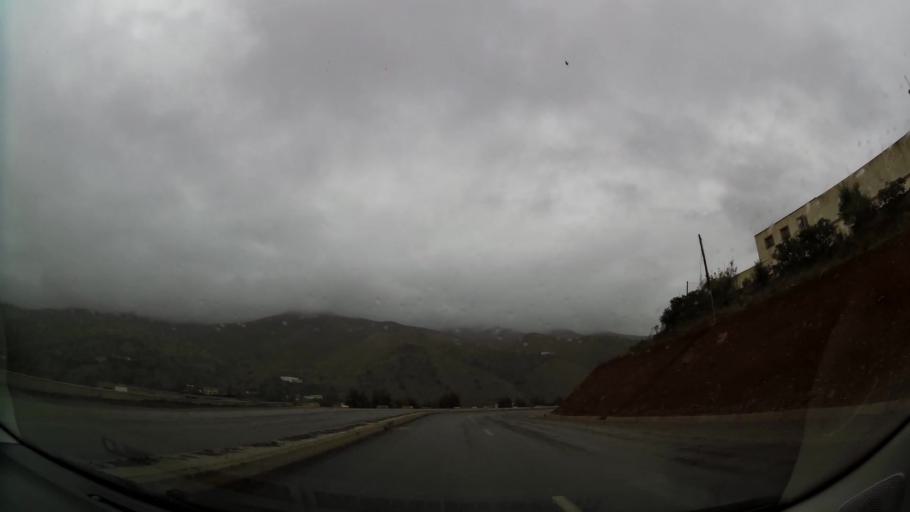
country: MA
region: Taza-Al Hoceima-Taounate
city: Imzourene
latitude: 35.0222
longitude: -3.8208
